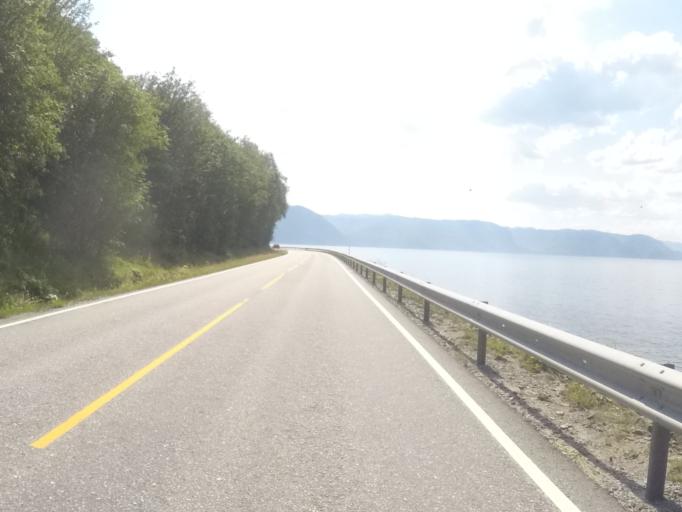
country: NO
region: Sogn og Fjordane
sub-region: Gaular
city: Sande
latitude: 61.1493
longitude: 5.6246
